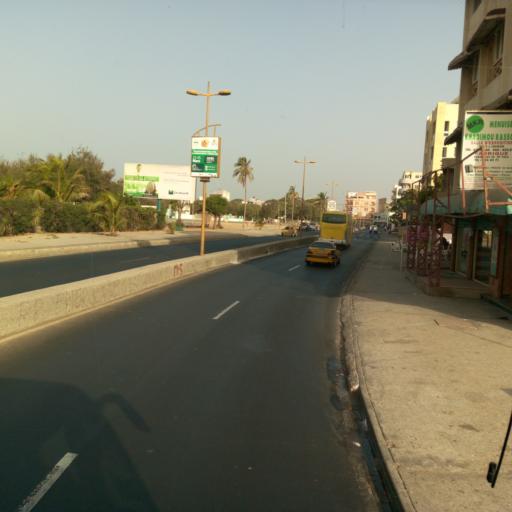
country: SN
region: Dakar
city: Dakar
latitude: 14.6745
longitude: -17.4523
